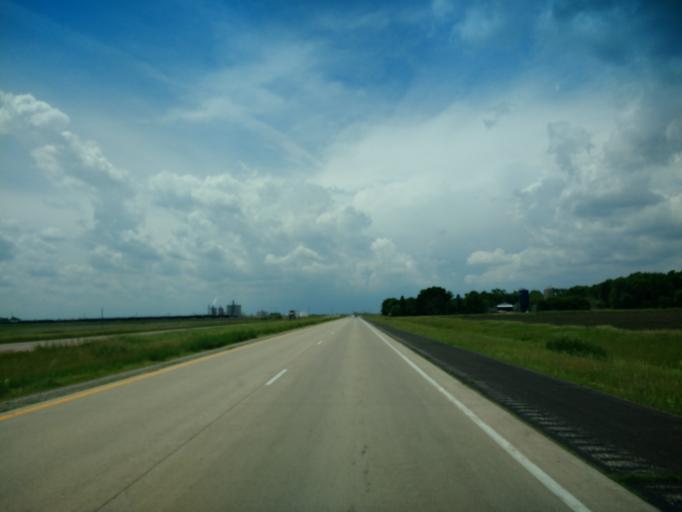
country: US
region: Minnesota
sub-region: Cottonwood County
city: Windom
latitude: 43.8140
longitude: -95.2693
